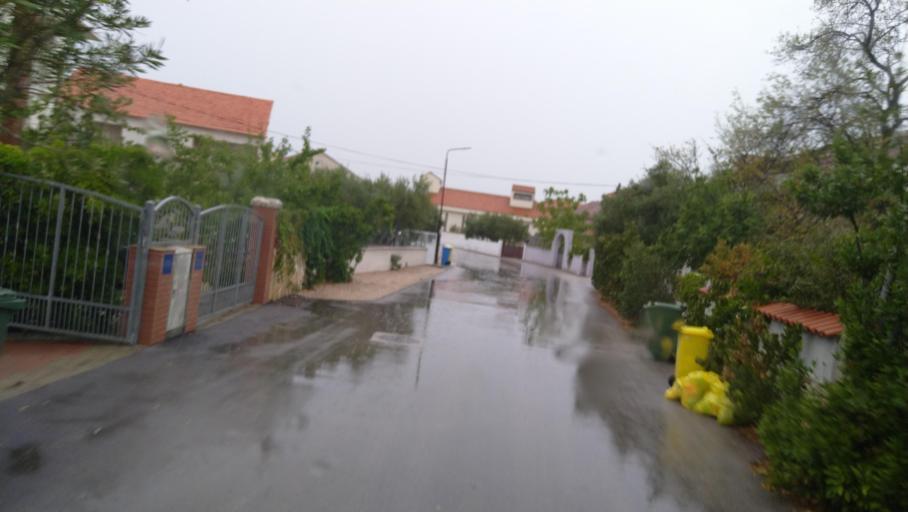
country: HR
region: Sibensko-Kniniska
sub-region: Grad Sibenik
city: Brodarica
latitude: 43.6778
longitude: 15.9196
